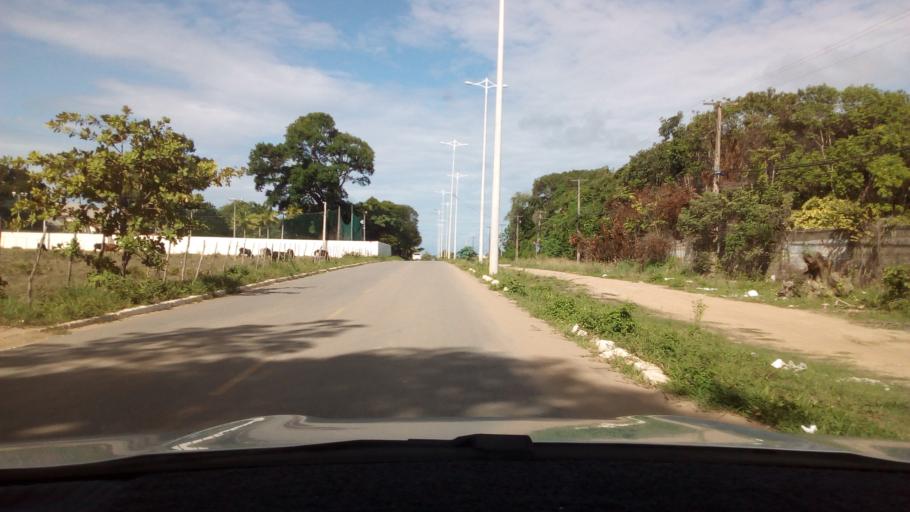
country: BR
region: Paraiba
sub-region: Joao Pessoa
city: Joao Pessoa
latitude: -7.1352
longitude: -34.8260
